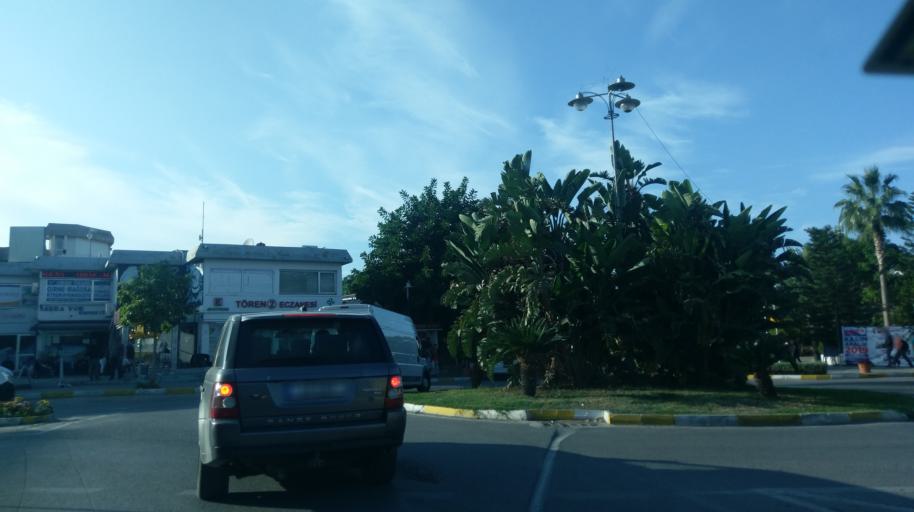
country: CY
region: Keryneia
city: Kyrenia
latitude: 35.3395
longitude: 33.3207
